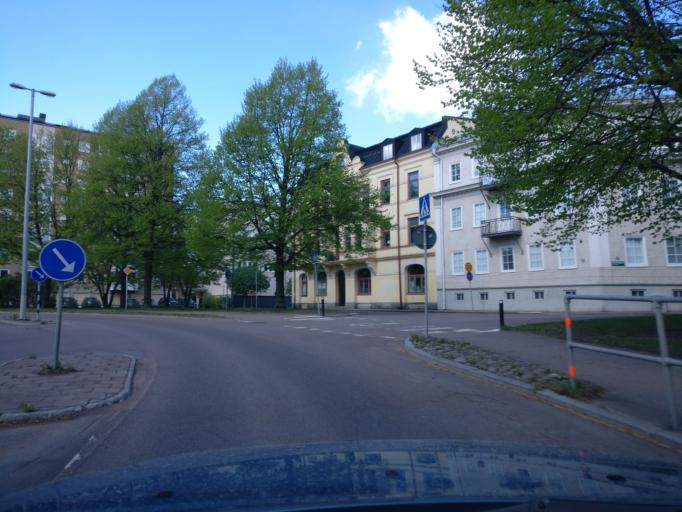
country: SE
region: Vaermland
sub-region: Karlstads Kommun
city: Karlstad
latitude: 59.3821
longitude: 13.5167
